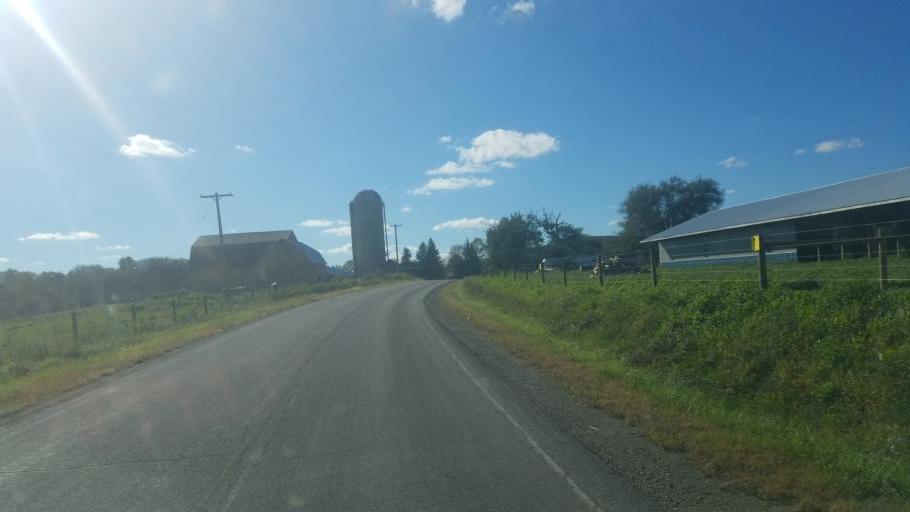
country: US
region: New York
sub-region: Allegany County
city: Cuba
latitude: 42.2743
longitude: -78.2060
